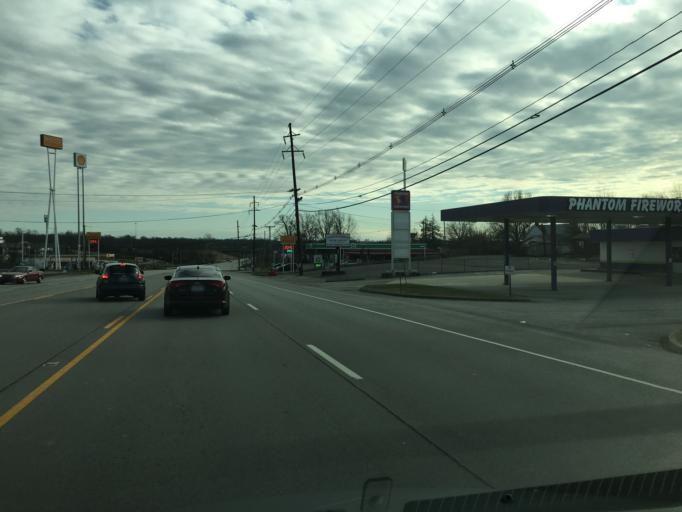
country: US
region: Kentucky
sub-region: Franklin County
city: Frankfort
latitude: 38.1792
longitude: -84.8146
